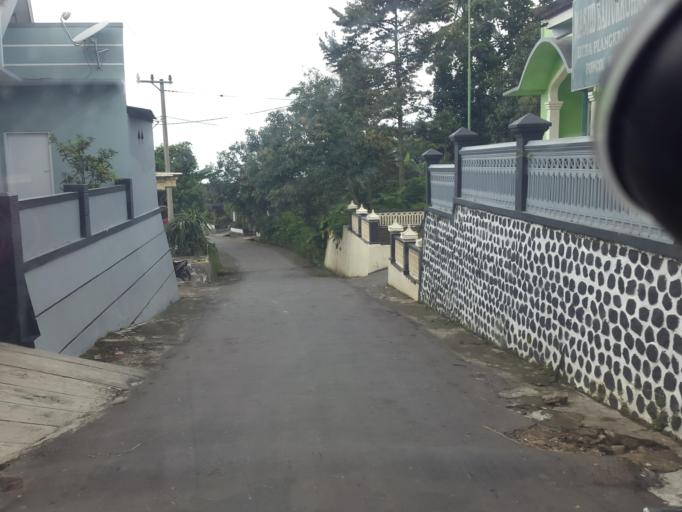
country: ID
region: Central Java
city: Jatiroto
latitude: -7.7024
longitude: 111.2788
